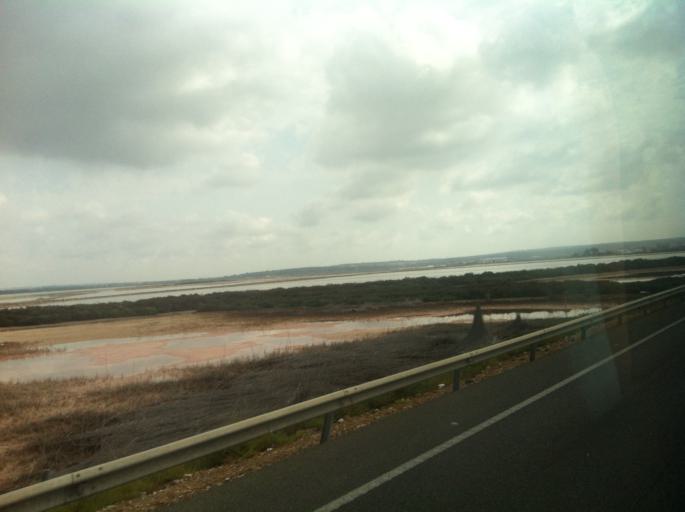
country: ES
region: Valencia
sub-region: Provincia de Alicante
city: Santa Pola
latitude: 38.1847
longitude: -0.6132
